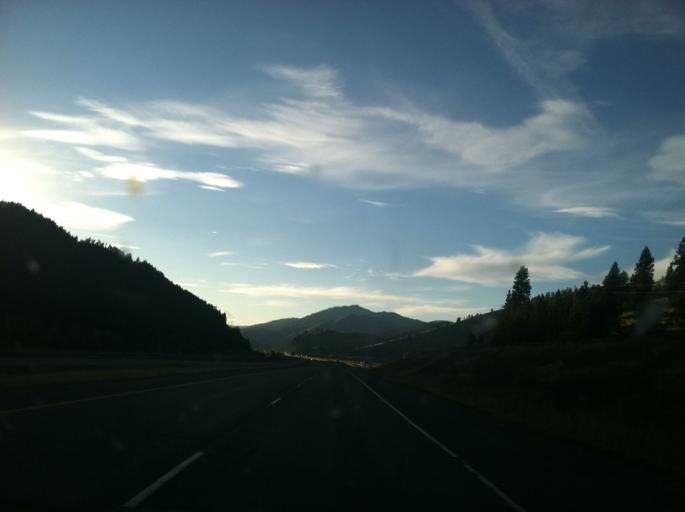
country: US
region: Montana
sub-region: Missoula County
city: Clinton
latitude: 46.7137
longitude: -113.5235
